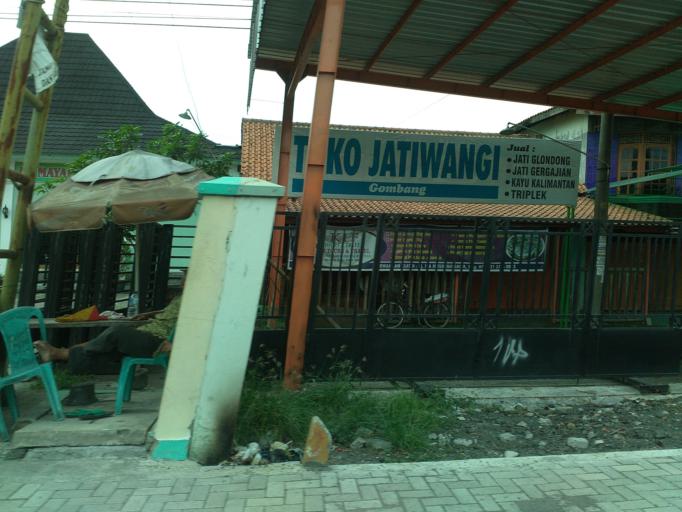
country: ID
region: Central Java
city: Trucuk
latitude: -7.6859
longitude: 110.6401
